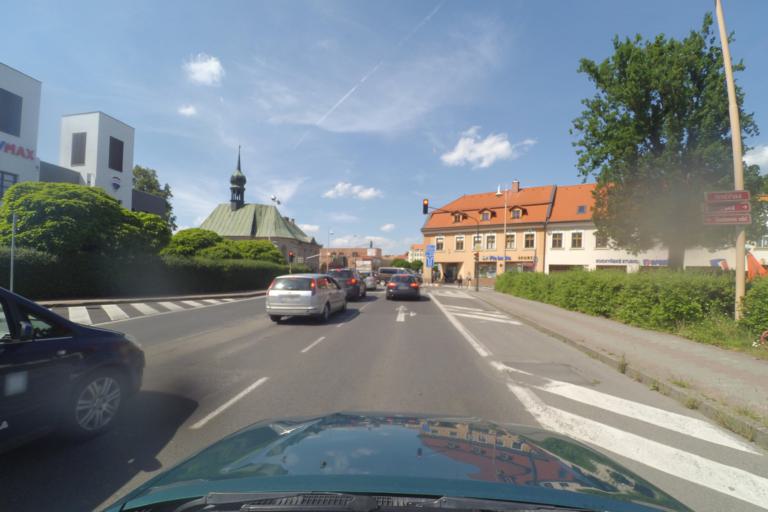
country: CZ
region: Liberecky
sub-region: Okres Ceska Lipa
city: Ceska Lipa
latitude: 50.6824
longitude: 14.5367
